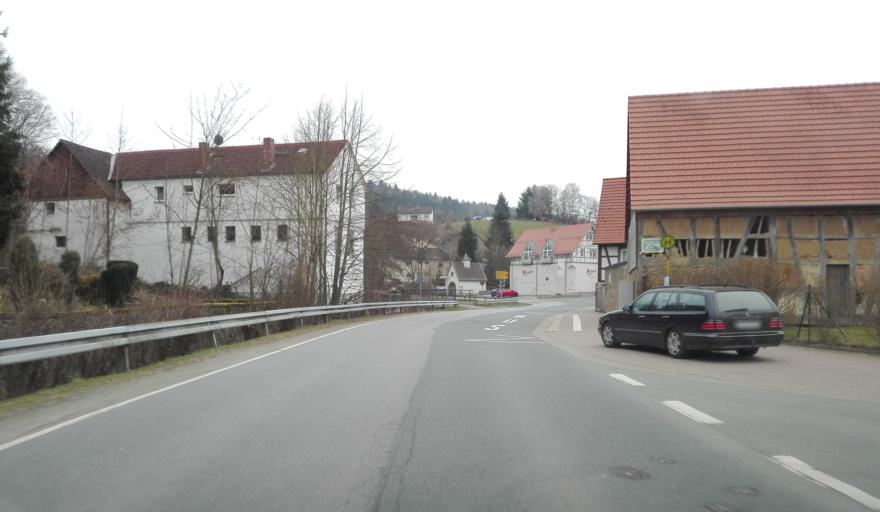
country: DE
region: Hesse
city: Lutzelbach
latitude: 49.7524
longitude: 8.7207
